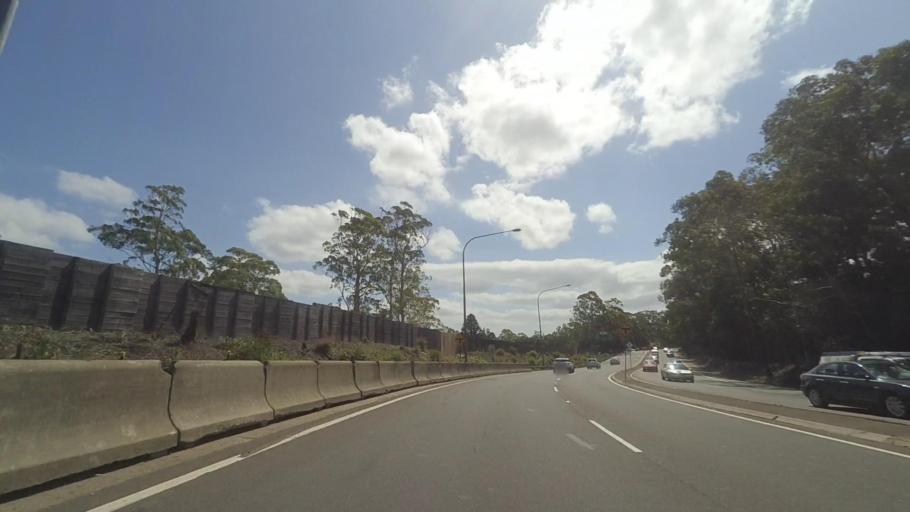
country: AU
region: New South Wales
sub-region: Ku-ring-gai
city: Normanhurst
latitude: -33.7203
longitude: 151.1087
